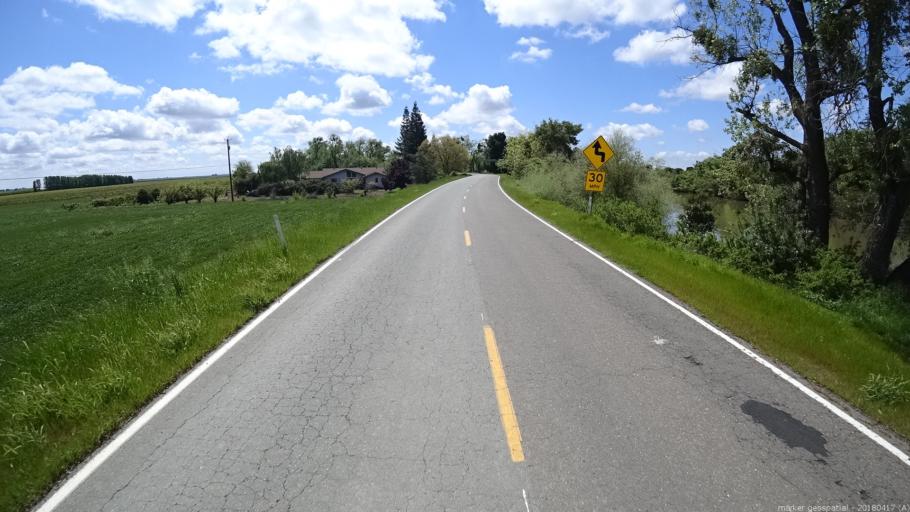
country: US
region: California
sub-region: Sacramento County
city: Walnut Grove
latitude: 38.2284
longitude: -121.5247
